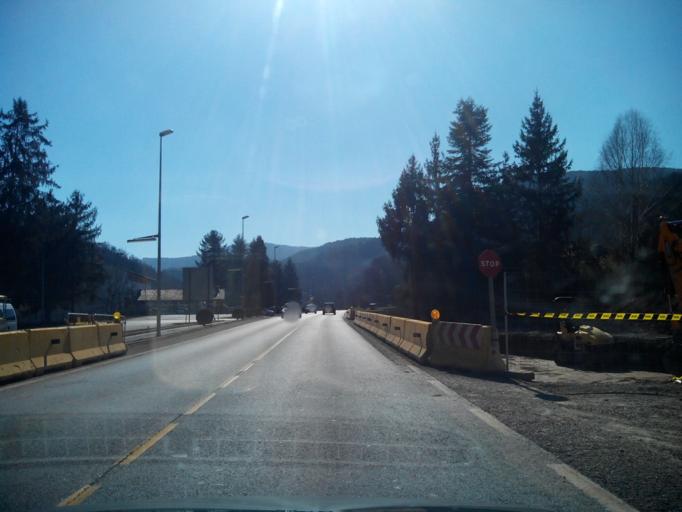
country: ES
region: Catalonia
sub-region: Provincia de Girona
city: Ripoll
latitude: 42.1840
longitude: 2.1959
